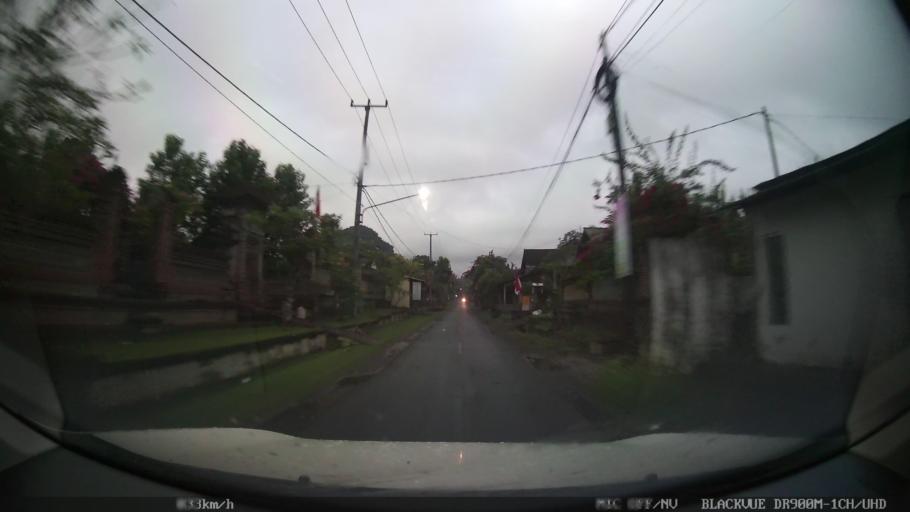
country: ID
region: Bali
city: Banjar Tebongkang
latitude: -8.5352
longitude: 115.2522
